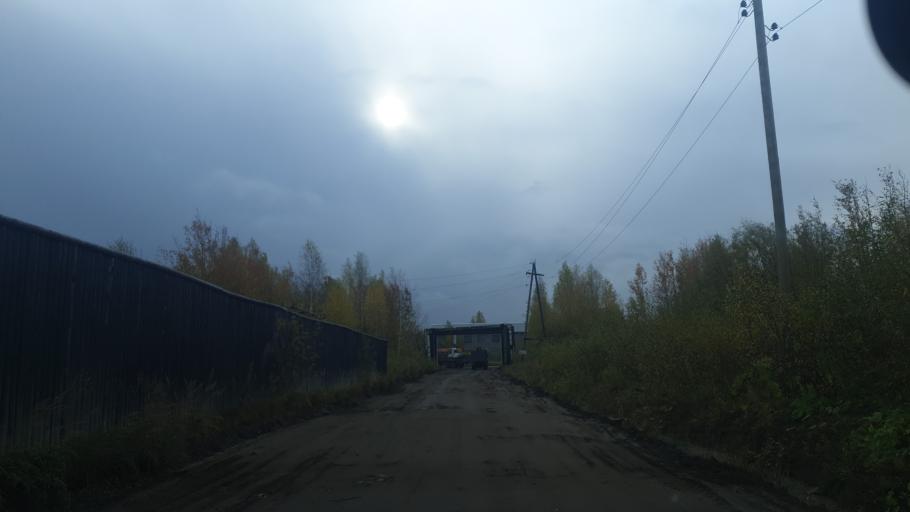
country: RU
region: Komi Republic
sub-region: Syktyvdinskiy Rayon
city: Syktyvkar
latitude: 61.7254
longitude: 50.7488
